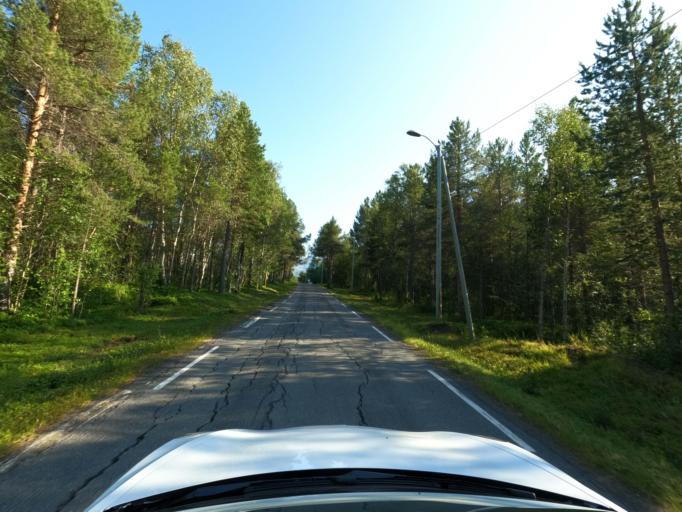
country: NO
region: Nordland
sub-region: Narvik
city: Bjerkvik
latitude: 68.4797
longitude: 17.5277
